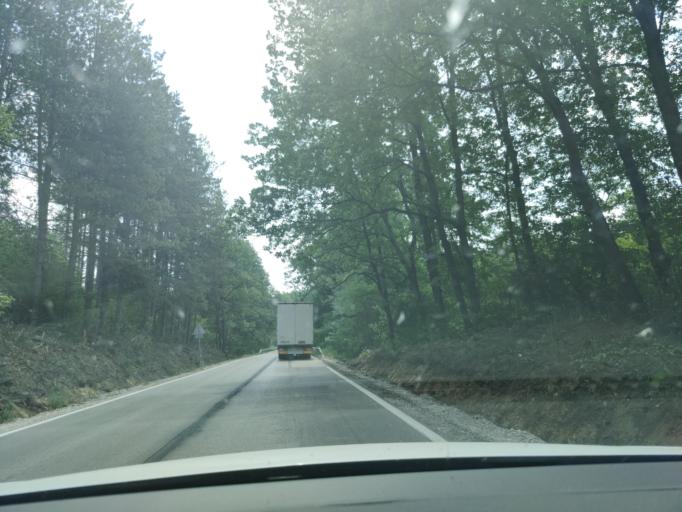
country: BG
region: Vidin
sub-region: Obshtina Dimovo
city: Dimovo
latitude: 43.6779
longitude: 22.7687
